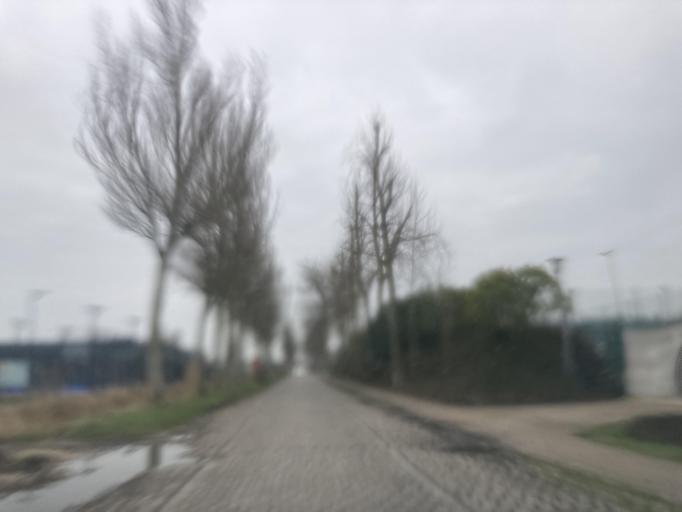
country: BE
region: Flanders
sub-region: Provincie West-Vlaanderen
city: Veurne
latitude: 51.0831
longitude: 2.6578
